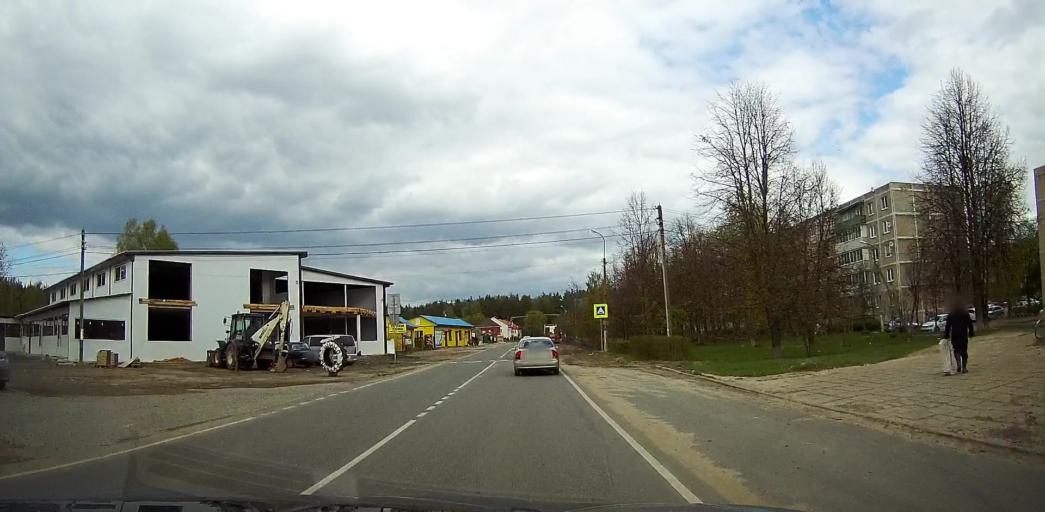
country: RU
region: Moskovskaya
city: Ashitkovo
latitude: 55.4367
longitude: 38.5792
